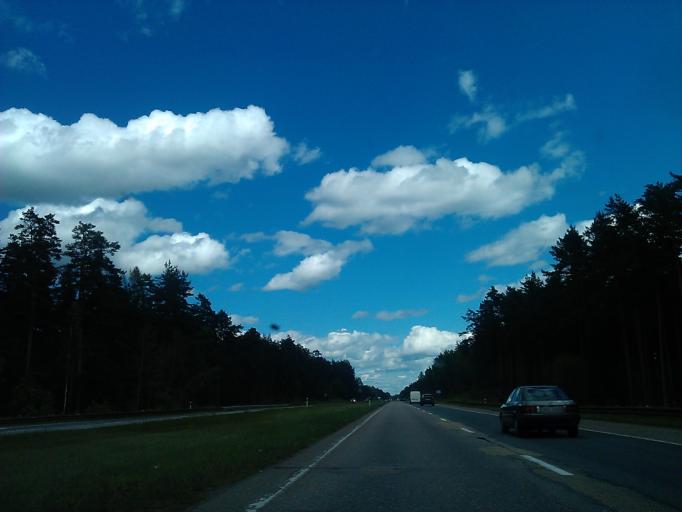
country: LV
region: Adazi
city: Adazi
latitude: 57.0266
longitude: 24.3597
